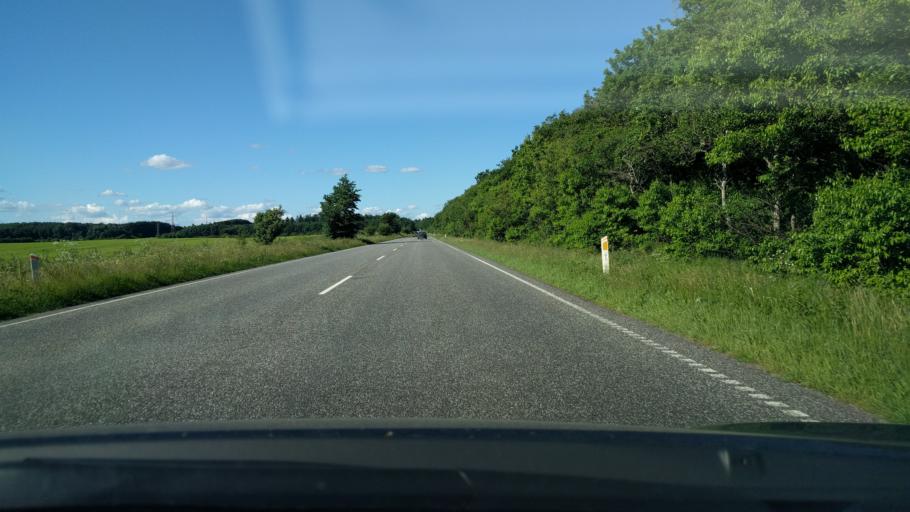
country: DK
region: North Denmark
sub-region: Vesthimmerland Kommune
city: Alestrup
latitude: 56.6272
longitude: 9.5142
